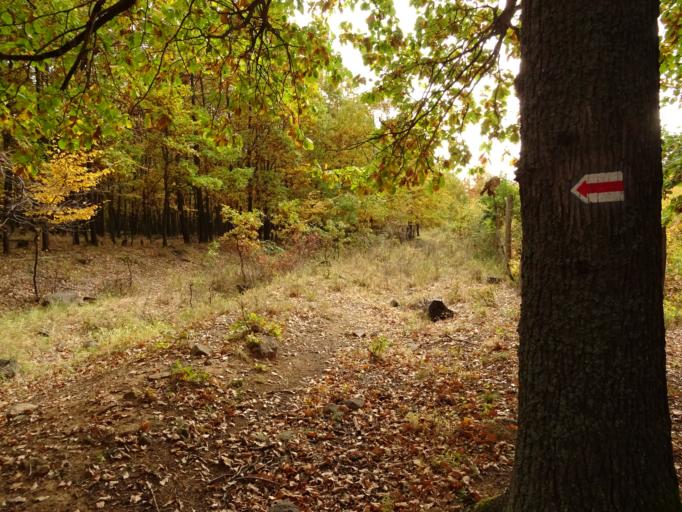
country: HU
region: Heves
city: Gyongyostarjan
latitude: 47.8744
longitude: 19.8886
